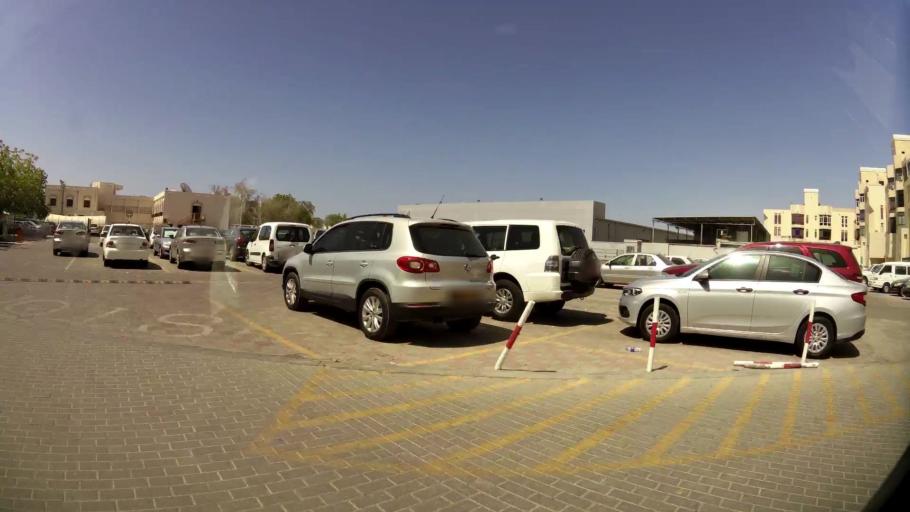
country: OM
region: Muhafazat Masqat
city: Bawshar
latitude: 23.5900
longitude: 58.3623
